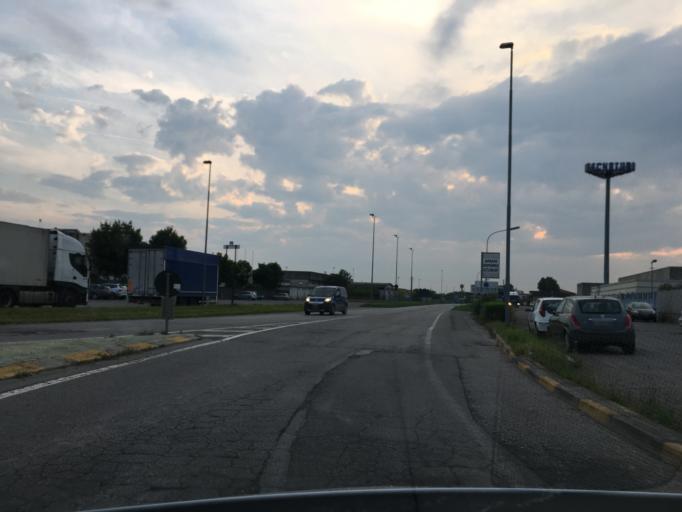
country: IT
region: Lombardy
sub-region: Provincia di Brescia
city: Alfianello
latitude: 45.2689
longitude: 10.1374
